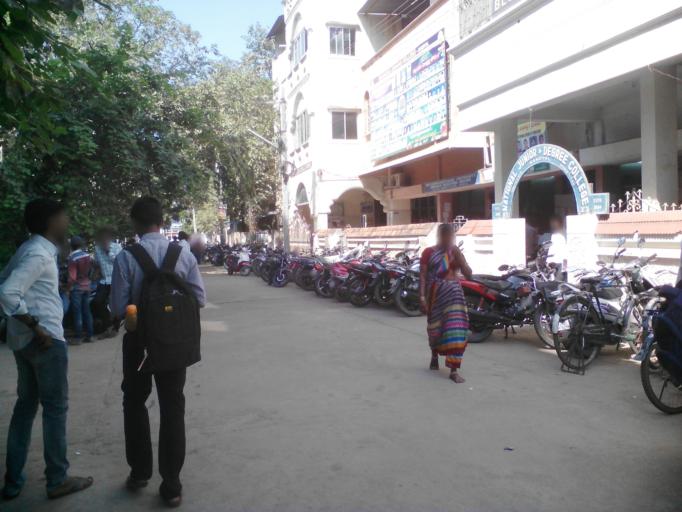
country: IN
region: Andhra Pradesh
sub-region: Kurnool
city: Nandyal
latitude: 15.4842
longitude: 78.4849
